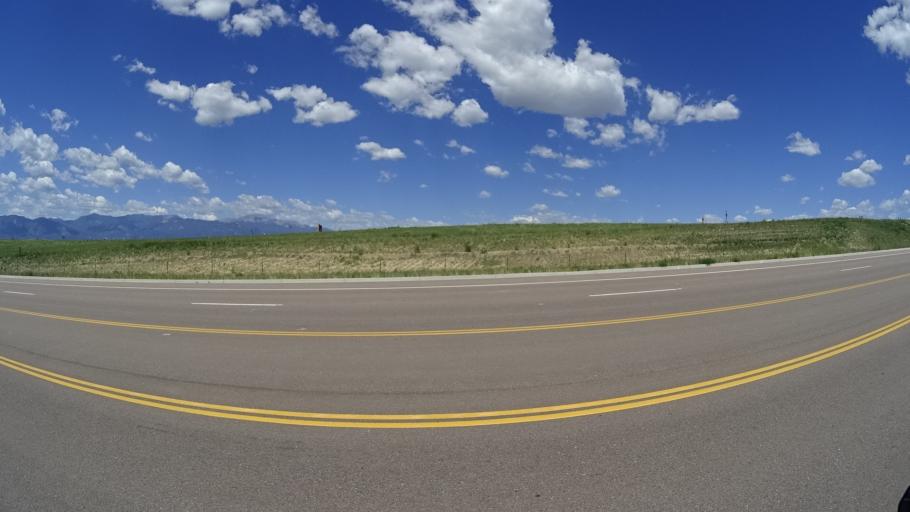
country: US
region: Colorado
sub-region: El Paso County
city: Cimarron Hills
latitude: 38.8491
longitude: -104.6825
